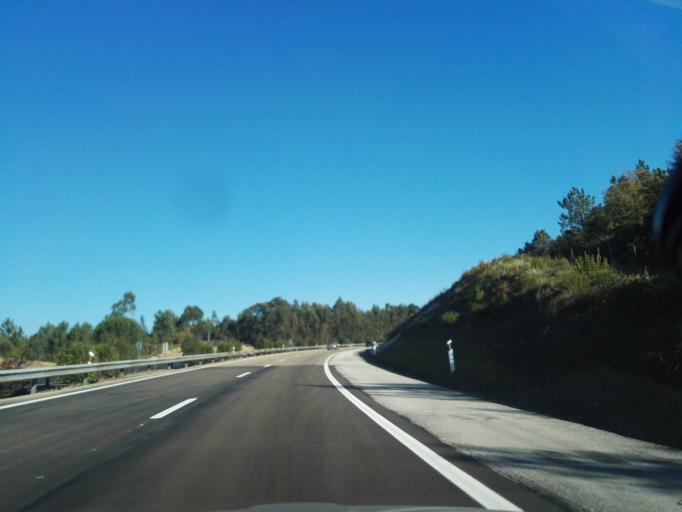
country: PT
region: Santarem
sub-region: Entroncamento
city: Entroncamento
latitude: 39.4902
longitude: -8.4411
